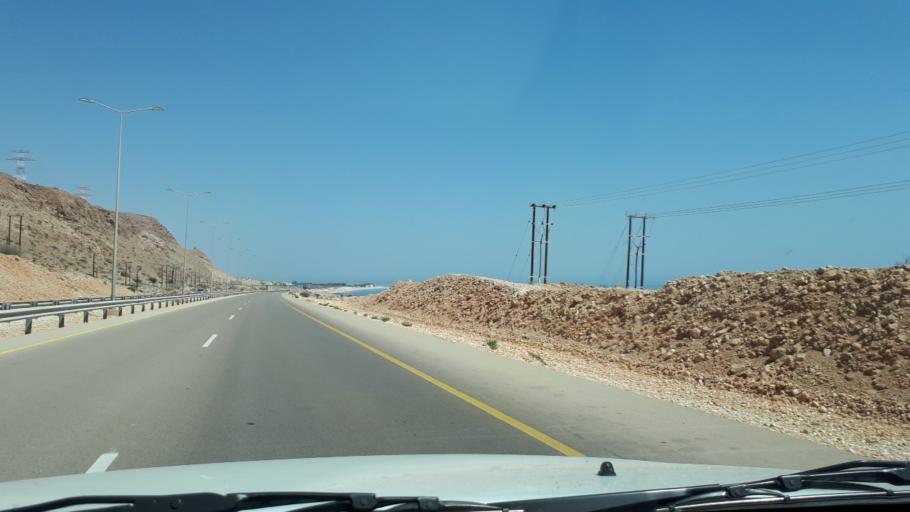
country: OM
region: Ash Sharqiyah
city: Sur
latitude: 22.8052
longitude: 59.2684
